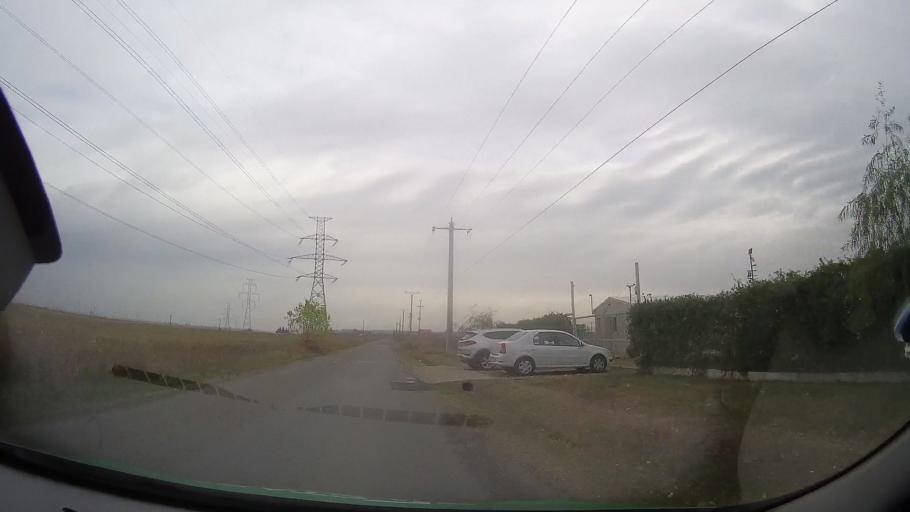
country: RO
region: Prahova
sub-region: Comuna Valea Calugareasca
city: Pantazi
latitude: 44.9271
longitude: 26.1509
